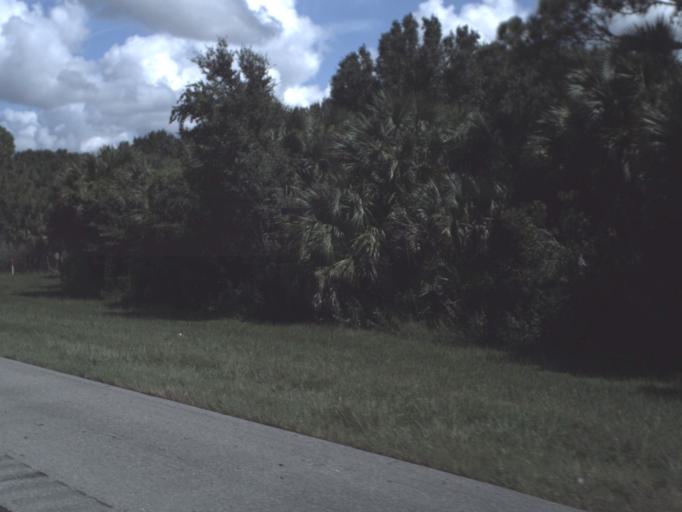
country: US
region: Florida
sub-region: Sarasota County
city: Osprey
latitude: 27.2151
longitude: -82.4457
